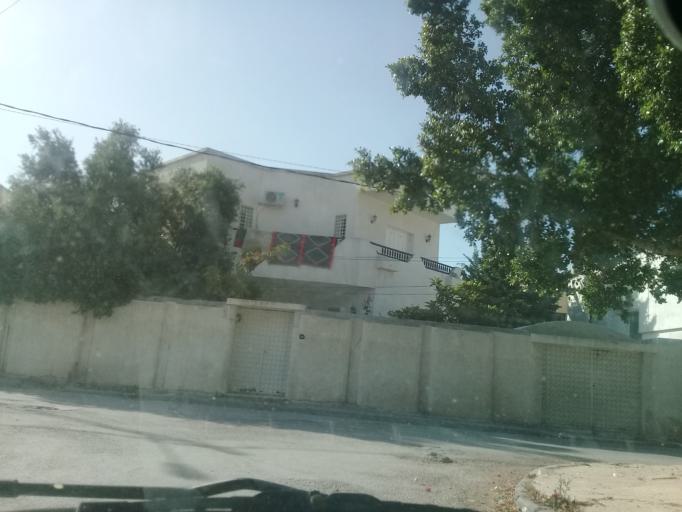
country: TN
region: Ariana
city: Ariana
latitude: 36.8345
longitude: 10.1952
